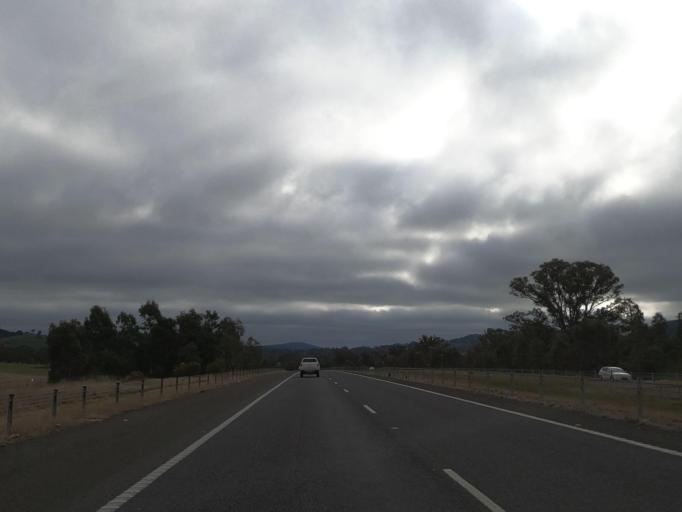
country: AU
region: Victoria
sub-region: Mount Alexander
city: Castlemaine
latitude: -37.0558
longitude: 144.3002
